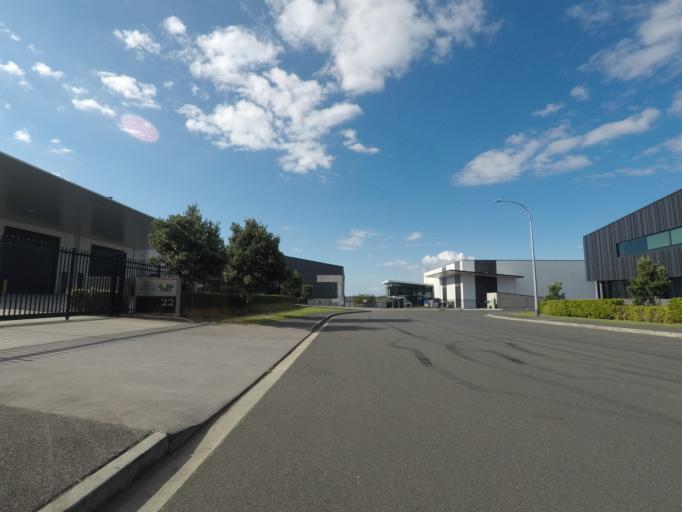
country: NZ
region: Auckland
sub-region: Auckland
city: Rosebank
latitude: -36.8822
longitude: 174.6837
